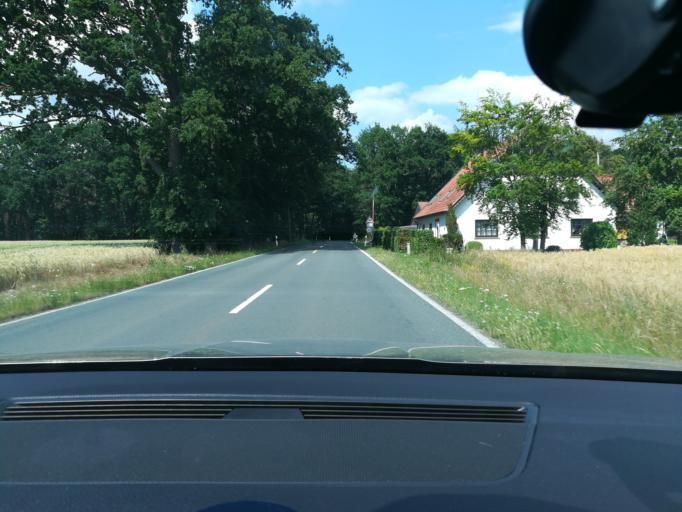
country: DE
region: North Rhine-Westphalia
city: Espelkamp
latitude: 52.3684
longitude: 8.6823
